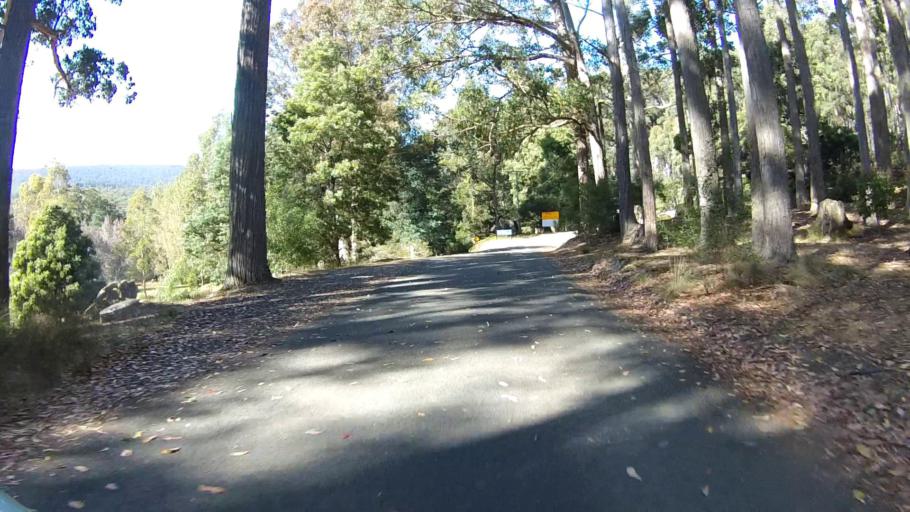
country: AU
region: Tasmania
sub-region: Derwent Valley
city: New Norfolk
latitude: -42.6828
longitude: 146.7159
